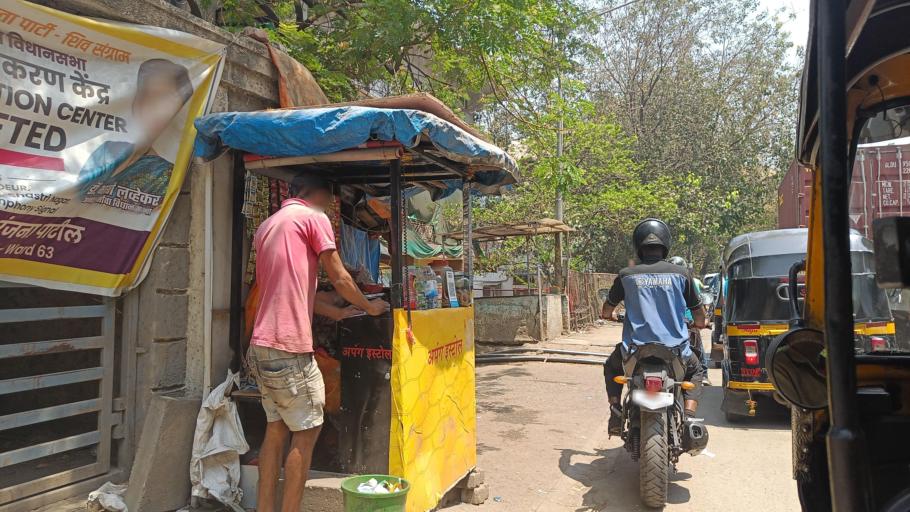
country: IN
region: Maharashtra
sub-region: Mumbai Suburban
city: Powai
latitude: 19.1380
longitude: 72.8426
